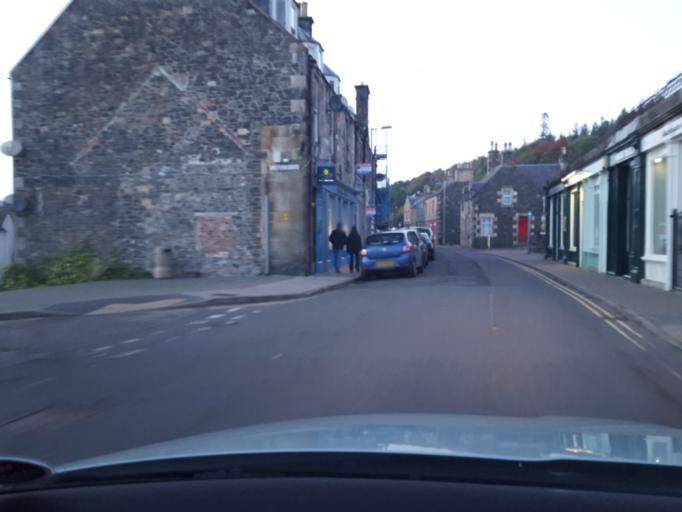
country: GB
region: Scotland
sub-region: The Scottish Borders
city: Peebles
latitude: 55.6533
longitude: -3.1890
